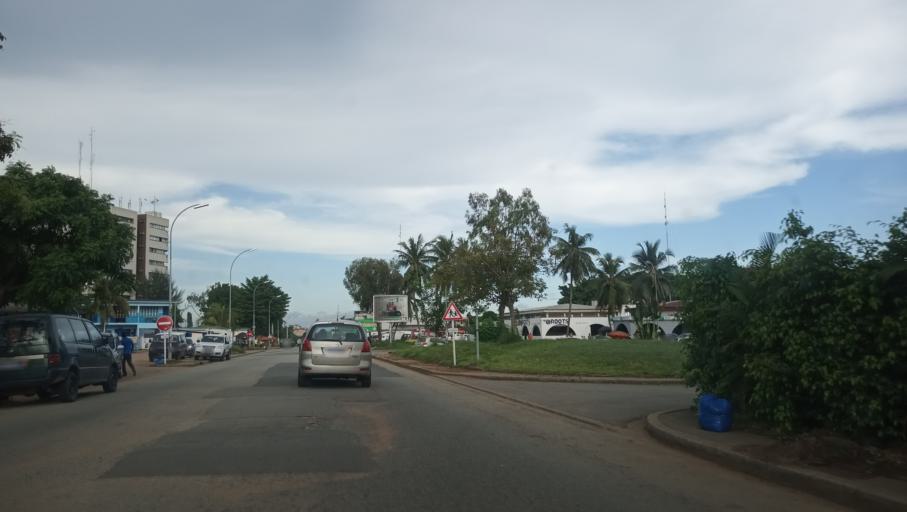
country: CI
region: Lagunes
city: Abidjan
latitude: 5.3407
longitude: -3.9784
